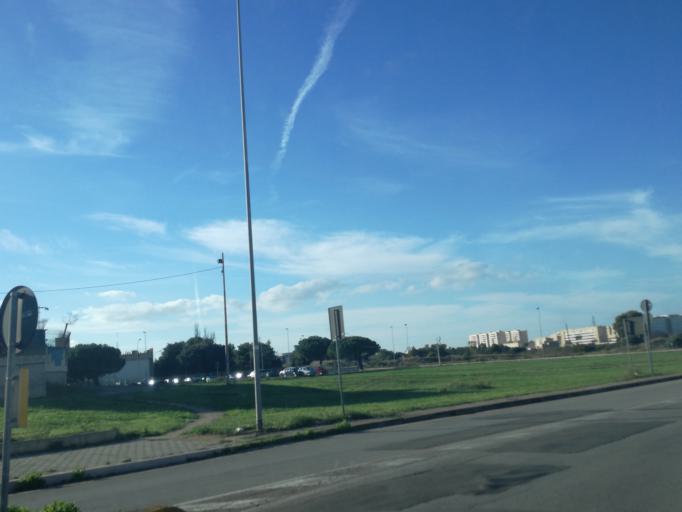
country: IT
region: Apulia
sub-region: Provincia di Bari
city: San Paolo
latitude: 41.1285
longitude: 16.7966
